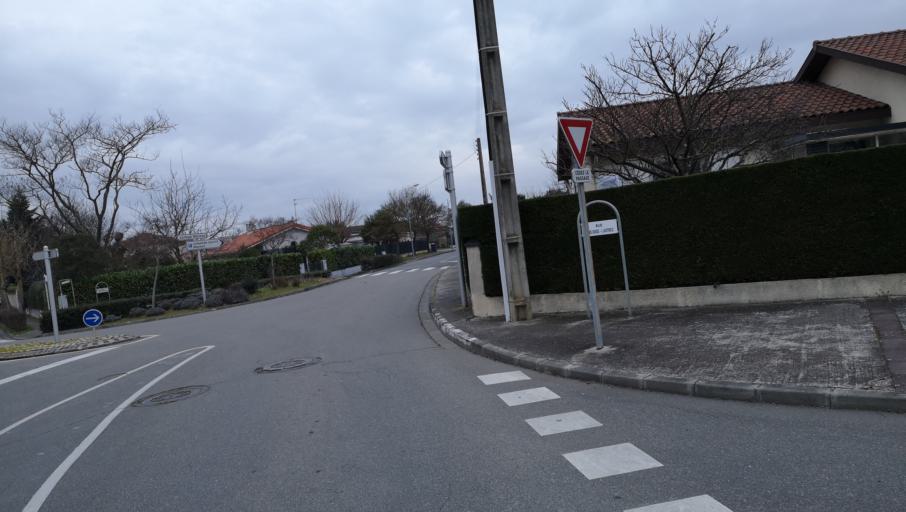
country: FR
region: Midi-Pyrenees
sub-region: Departement de la Haute-Garonne
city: Blagnac
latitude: 43.6430
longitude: 1.3829
